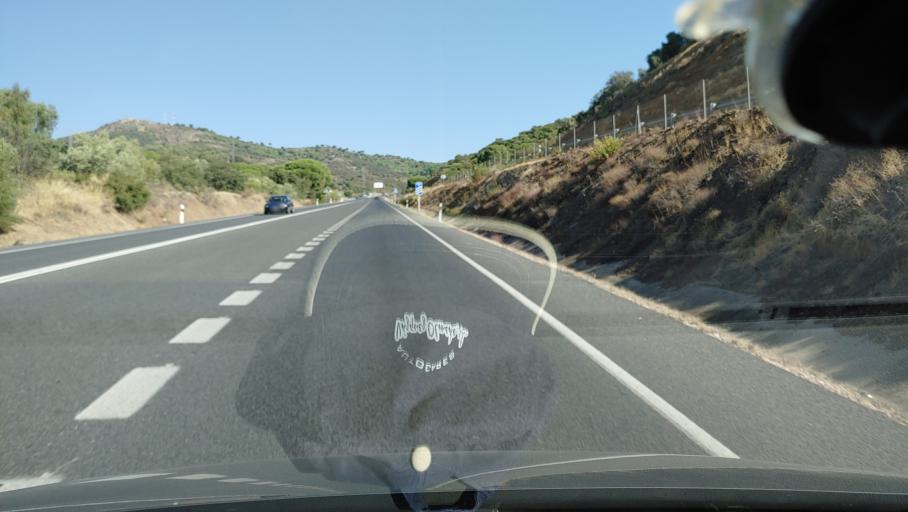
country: ES
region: Andalusia
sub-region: Province of Cordoba
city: Cordoba
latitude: 37.9681
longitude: -4.7686
